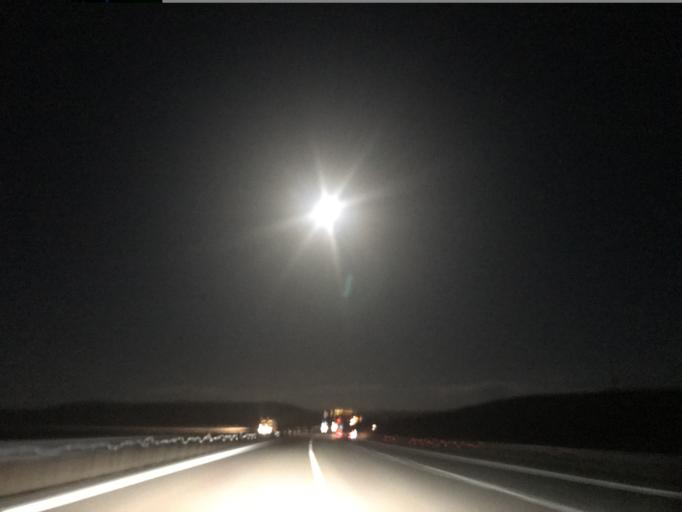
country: TR
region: Nigde
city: Ulukisla
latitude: 37.6355
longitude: 34.4335
